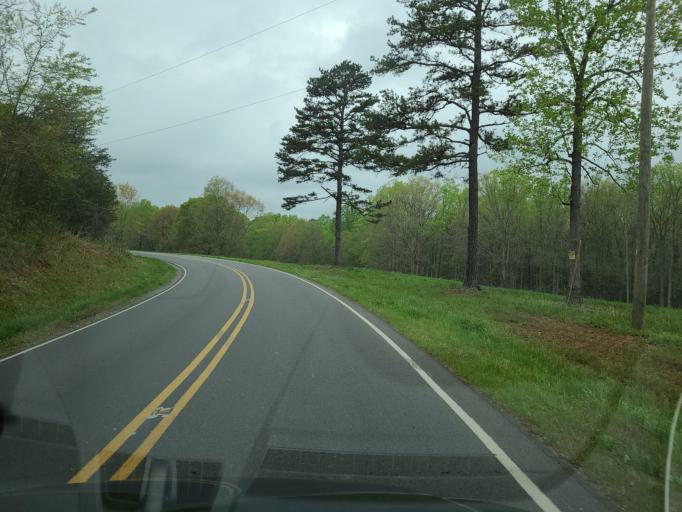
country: US
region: North Carolina
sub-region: Gaston County
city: Cherryville
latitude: 35.4387
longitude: -81.4154
